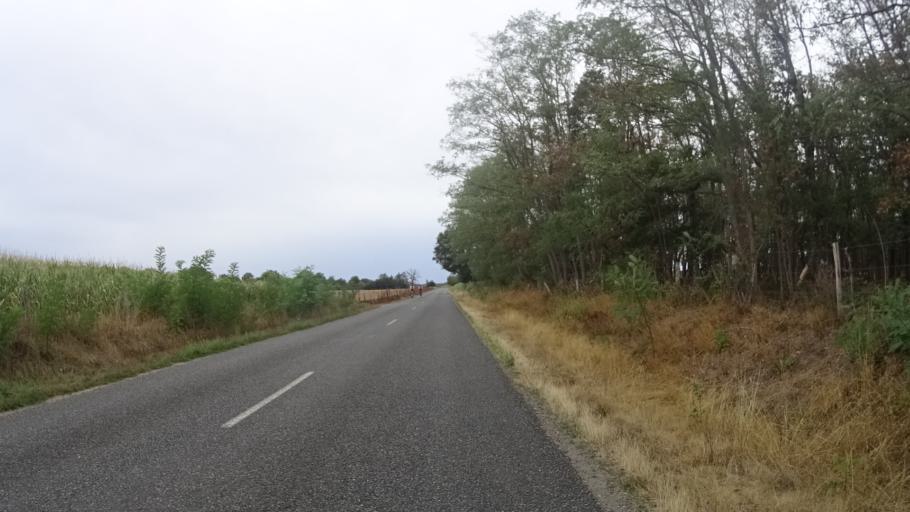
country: FR
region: Bourgogne
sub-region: Departement de la Nievre
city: Lucenay-les-Aix
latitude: 46.7699
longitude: 3.5535
